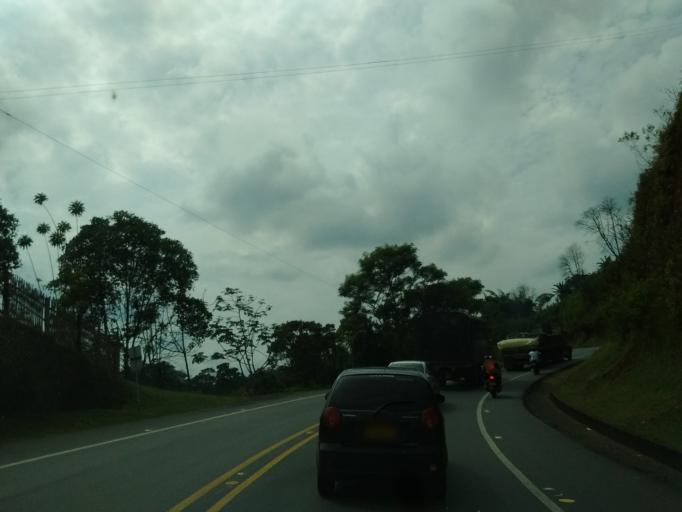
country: CO
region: Cauca
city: Caldono
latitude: 2.7921
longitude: -76.5508
